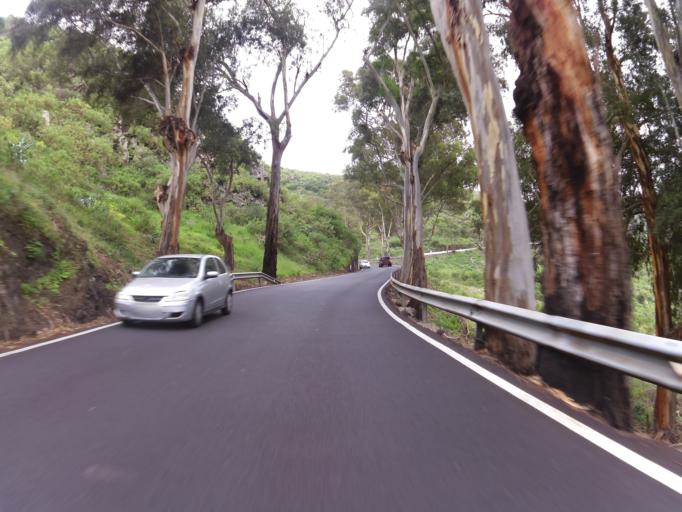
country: ES
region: Canary Islands
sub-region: Provincia de Las Palmas
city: Arucas
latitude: 28.0832
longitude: -15.5107
